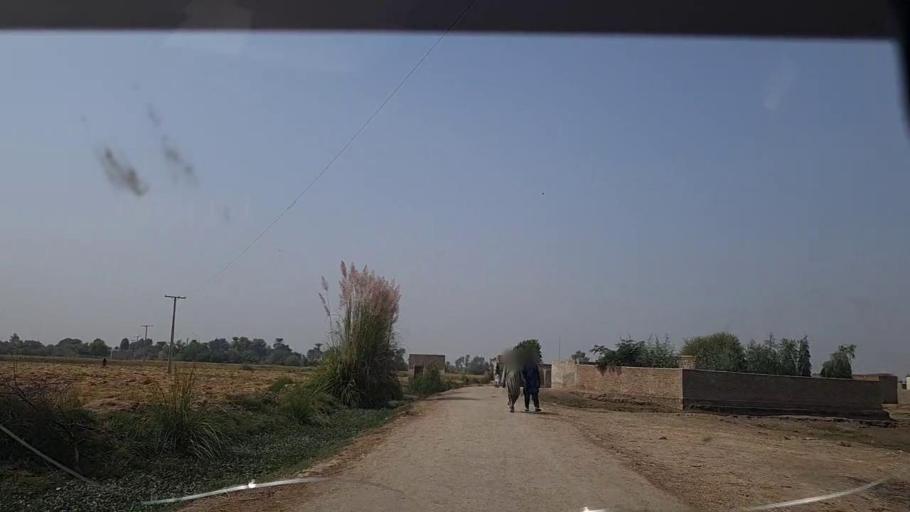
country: PK
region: Sindh
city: Shikarpur
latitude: 28.0902
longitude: 68.6742
